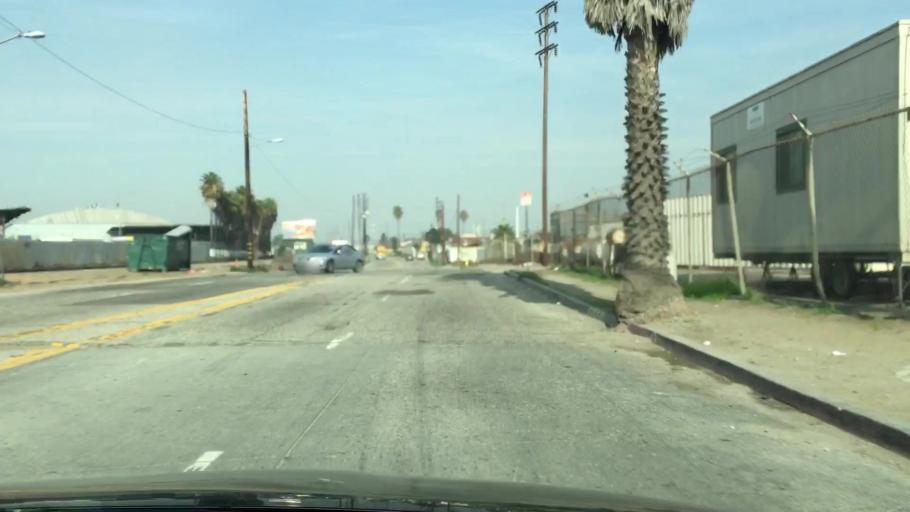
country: US
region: California
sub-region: Los Angeles County
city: Long Beach
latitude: 33.7817
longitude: -118.2447
